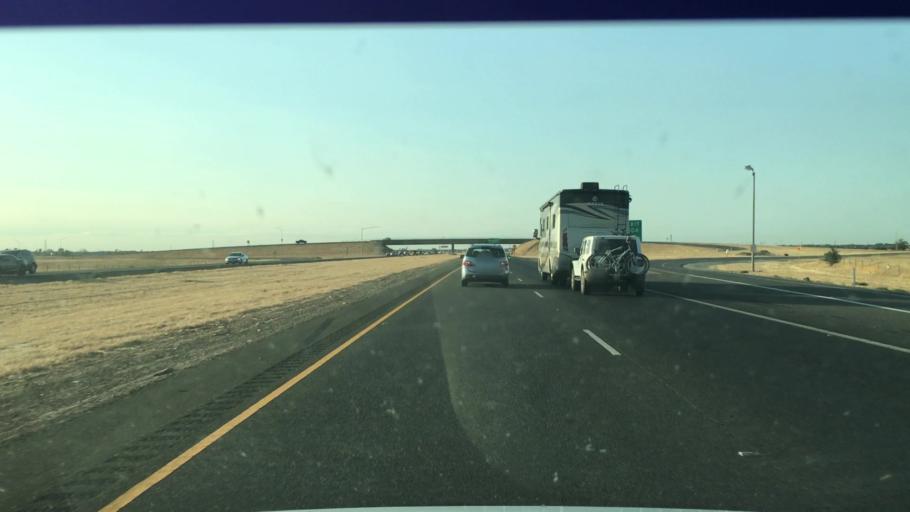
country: US
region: California
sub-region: Sacramento County
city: Laguna
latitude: 38.3714
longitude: -121.4758
